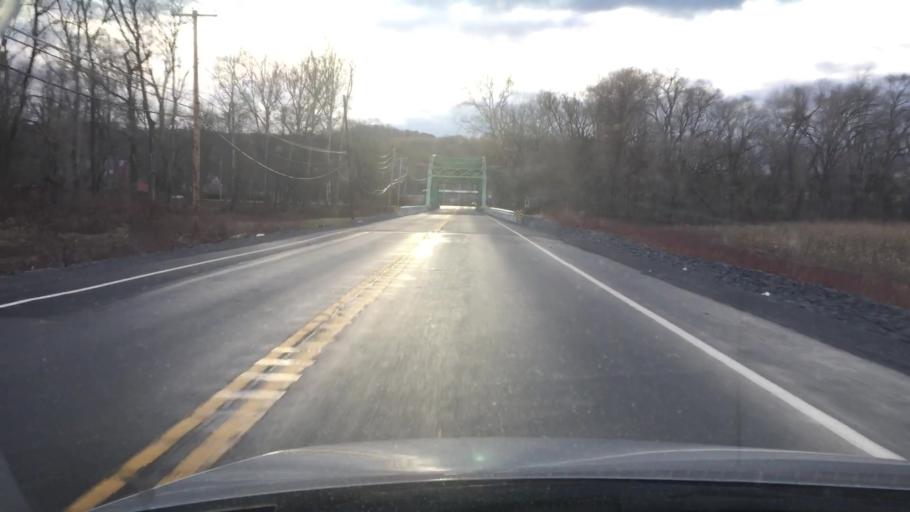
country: US
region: Pennsylvania
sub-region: Columbia County
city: Bloomsburg
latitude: 41.0230
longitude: -76.4749
